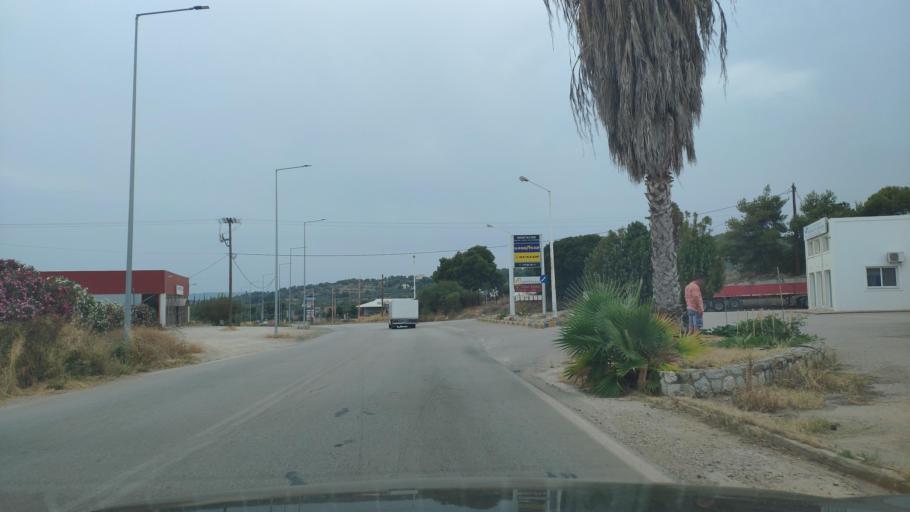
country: GR
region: Peloponnese
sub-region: Nomos Argolidos
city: Kranidi
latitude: 37.3544
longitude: 23.1586
